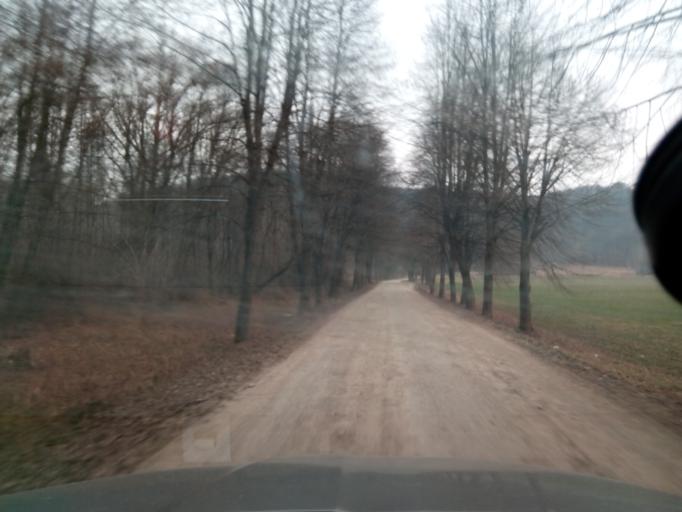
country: SK
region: Kosicky
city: Medzev
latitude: 48.6927
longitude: 20.9193
